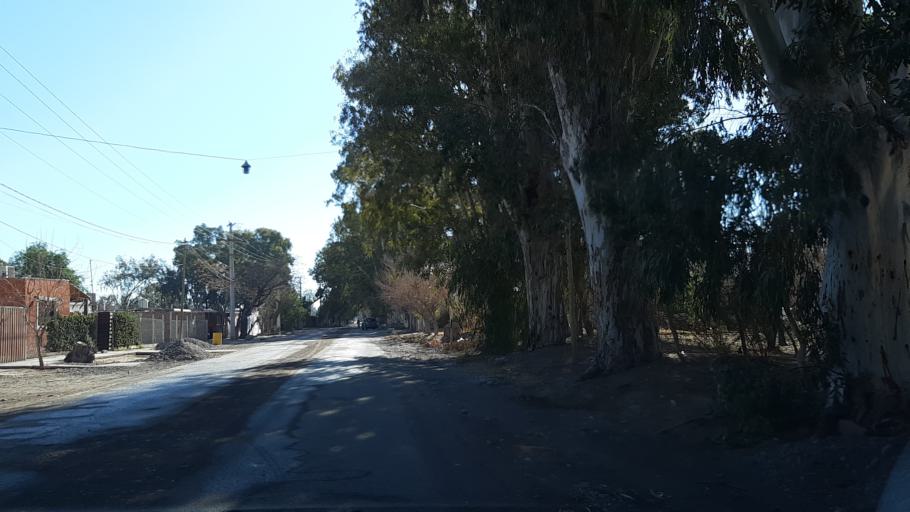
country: AR
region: San Juan
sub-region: Departamento de Zonda
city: Zonda
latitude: -31.5529
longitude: -68.7284
